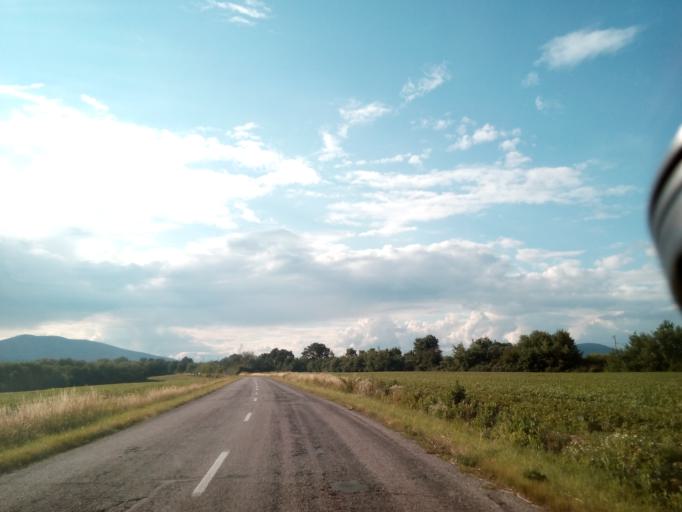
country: SK
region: Kosicky
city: Secovce
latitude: 48.6082
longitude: 21.5525
